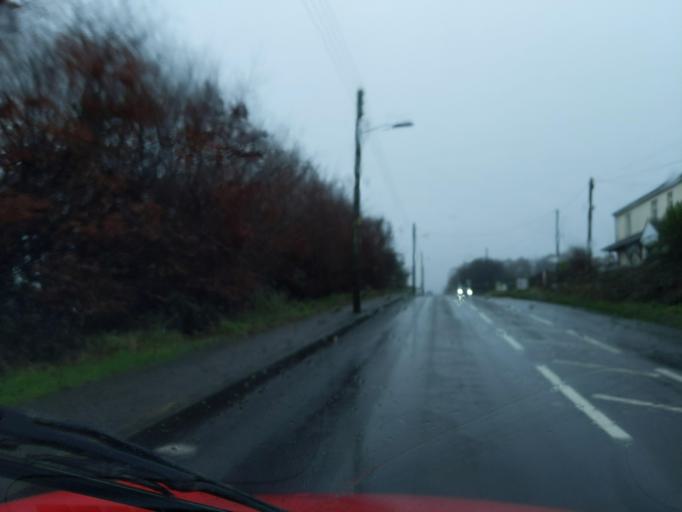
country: GB
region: England
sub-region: Cornwall
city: Callington
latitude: 50.5117
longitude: -4.3141
